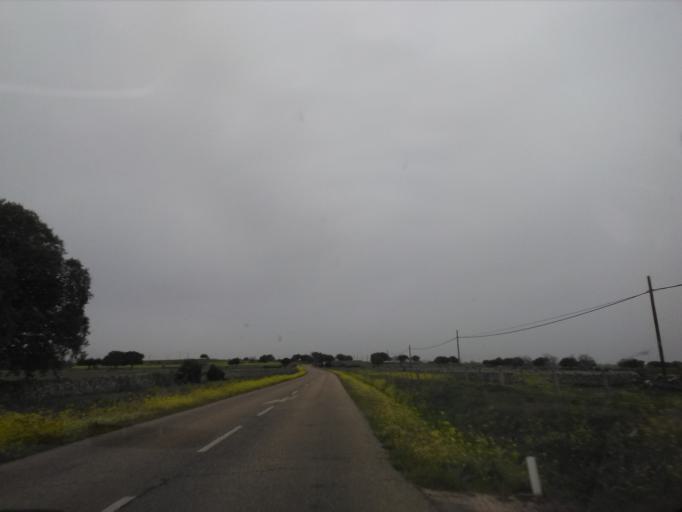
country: ES
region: Castille and Leon
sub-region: Provincia de Salamanca
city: Yecla de Yeltes
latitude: 40.9792
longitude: -6.4689
